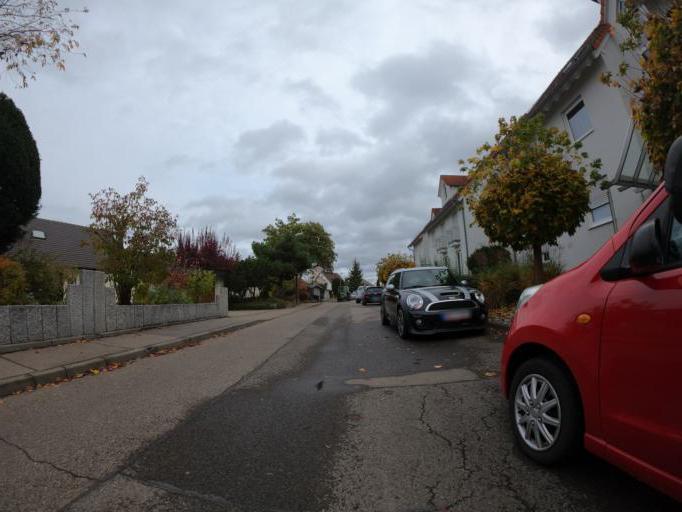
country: DE
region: Baden-Wuerttemberg
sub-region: Regierungsbezirk Stuttgart
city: Ehningen
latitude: 48.6948
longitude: 8.9365
